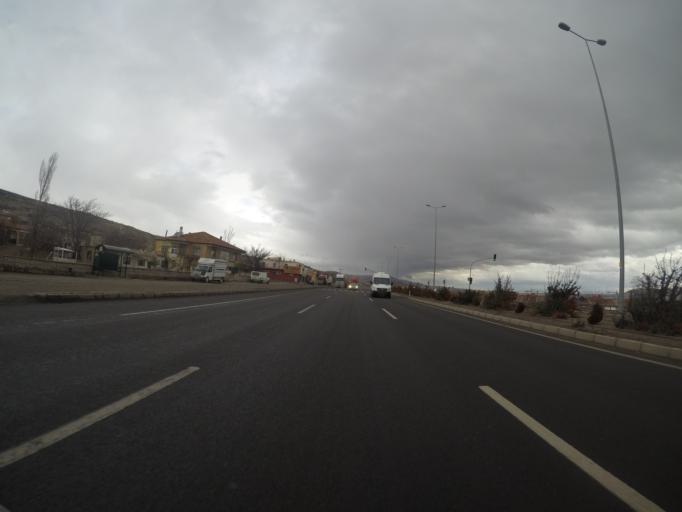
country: TR
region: Kayseri
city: Incesu
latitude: 38.7368
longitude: 35.2905
